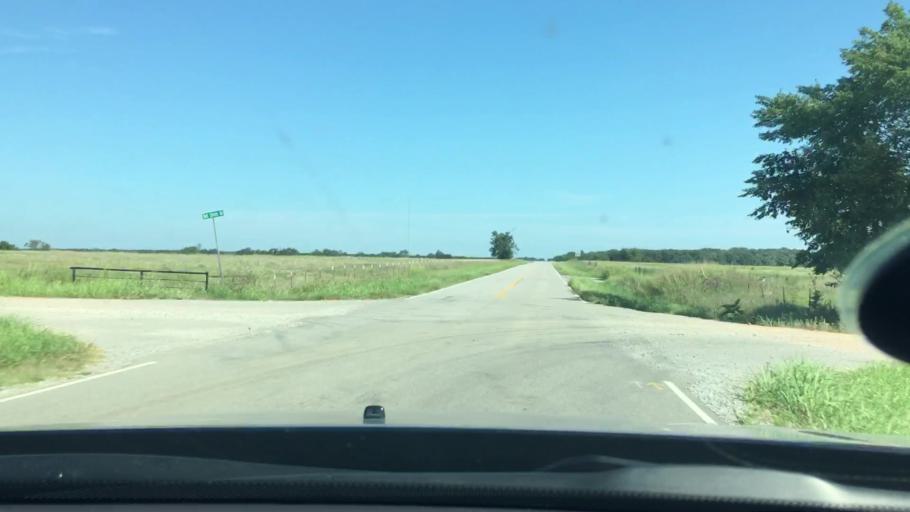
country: US
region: Oklahoma
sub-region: Johnston County
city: Tishomingo
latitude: 34.3030
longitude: -96.5488
